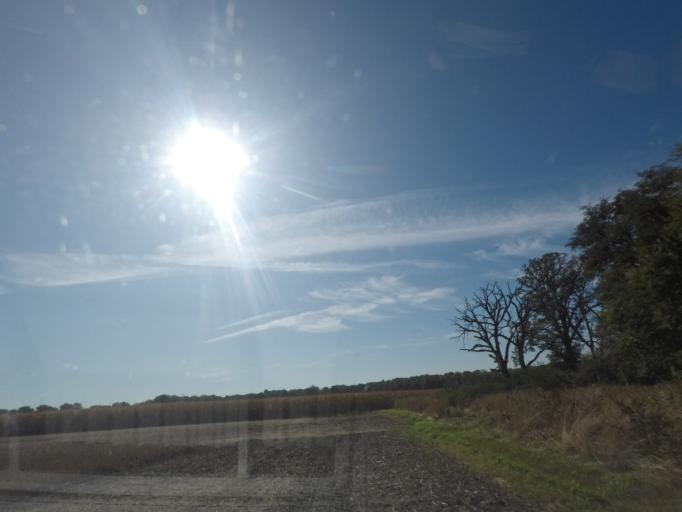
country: US
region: Iowa
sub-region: Story County
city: Nevada
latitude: 42.0303
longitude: -93.3764
